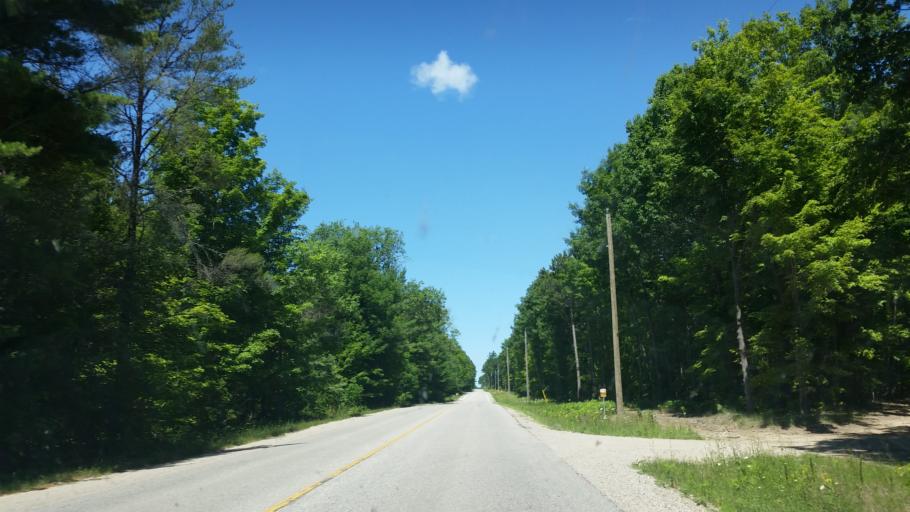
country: CA
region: Ontario
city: Barrie
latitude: 44.4745
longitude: -79.8071
